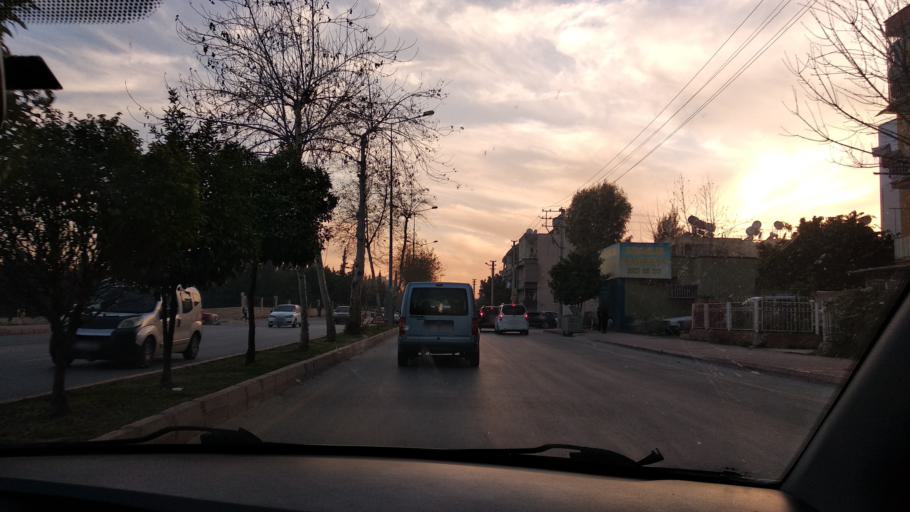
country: TR
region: Mersin
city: Mercin
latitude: 36.8235
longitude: 34.6016
